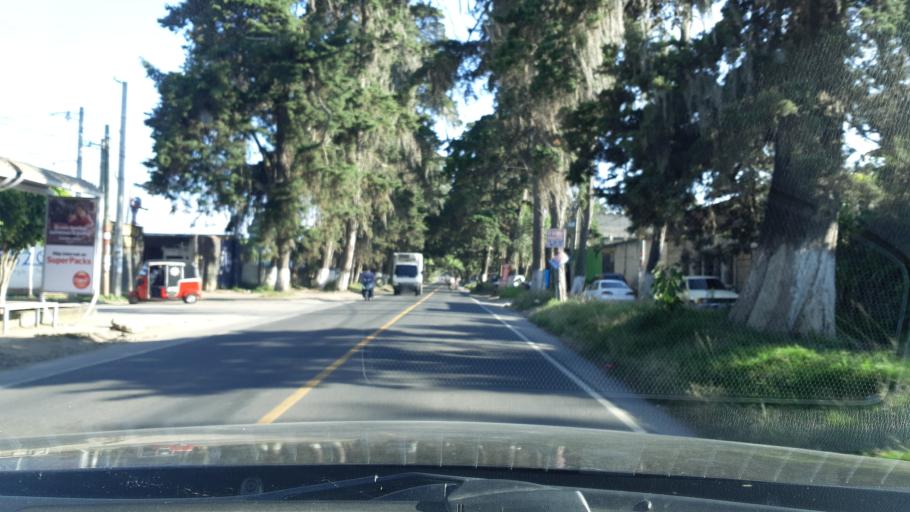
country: GT
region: Chimaltenango
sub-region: Municipio de Chimaltenango
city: Chimaltenango
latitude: 14.6468
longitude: -90.8123
